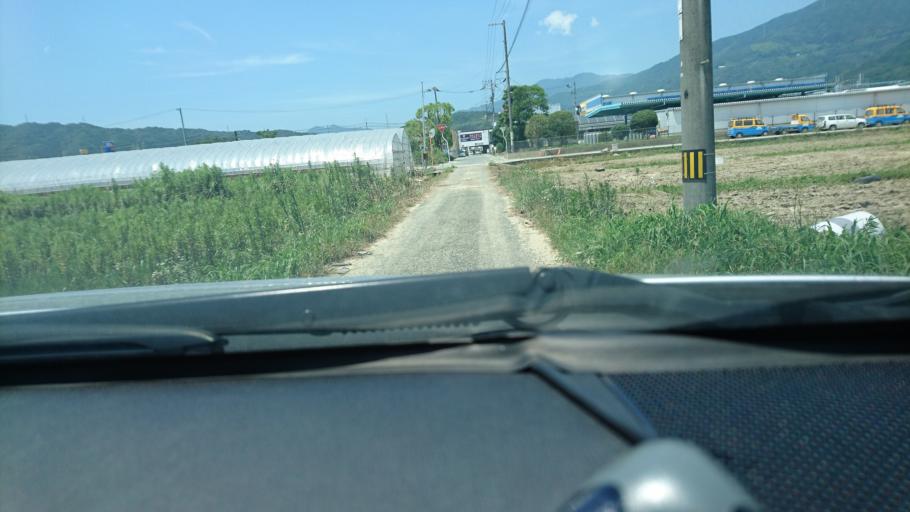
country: JP
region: Ehime
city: Ozu
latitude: 33.5262
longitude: 132.5675
